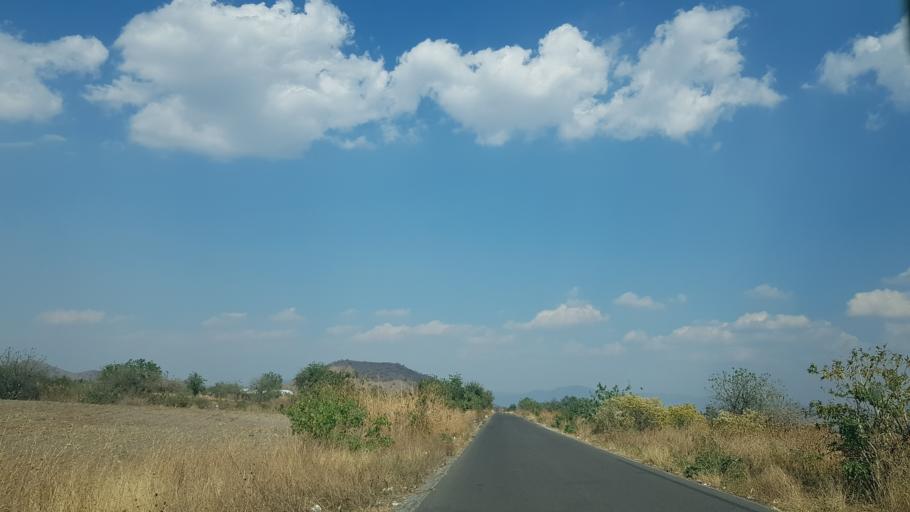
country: MX
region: Puebla
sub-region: Atlixco
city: Colonia Agricola de Ocotepec (Colonia San Jose)
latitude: 18.9236
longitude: -98.4963
